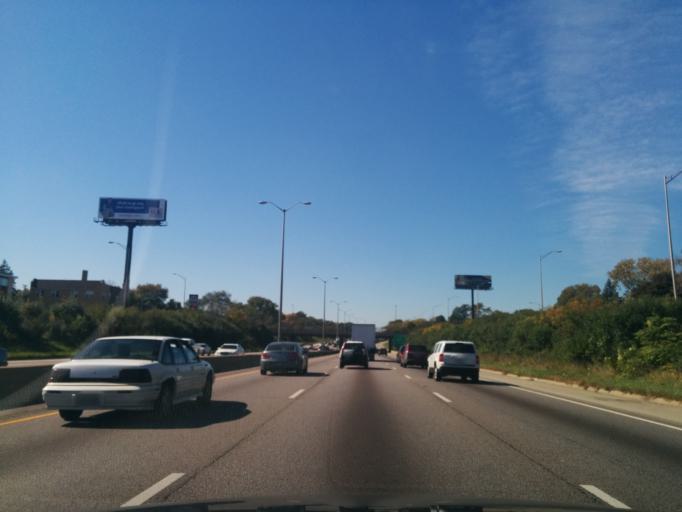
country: US
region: Illinois
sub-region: Cook County
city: Broadview
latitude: 41.8711
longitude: -87.8505
